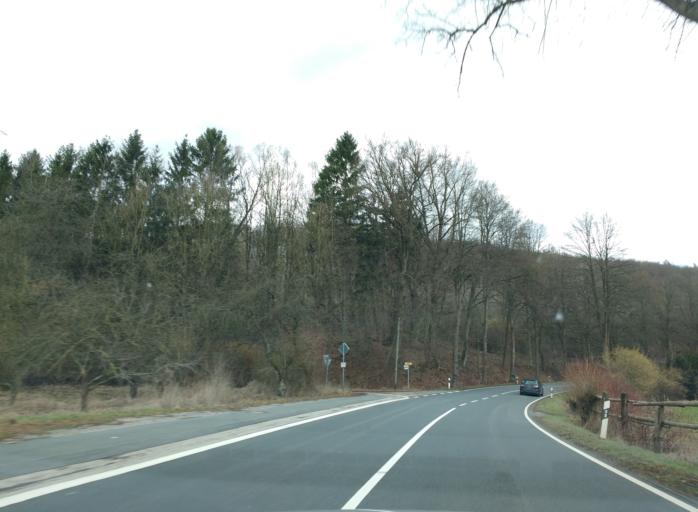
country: DE
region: North Rhine-Westphalia
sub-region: Regierungsbezirk Detmold
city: Lemgo
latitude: 52.0699
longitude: 8.9177
